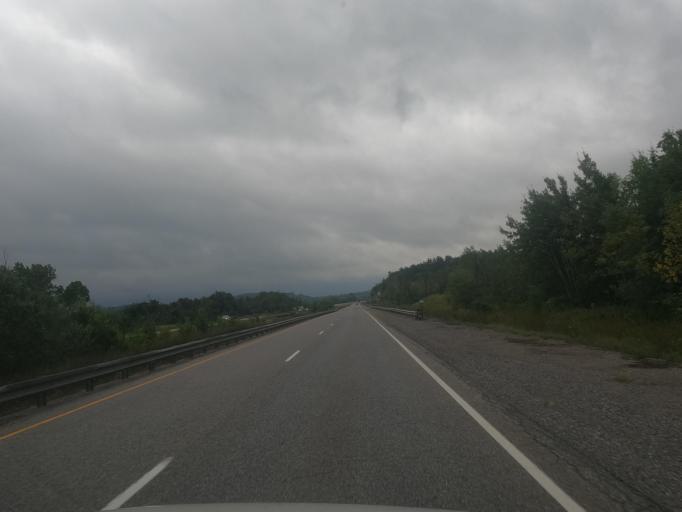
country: CA
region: Ontario
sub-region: Algoma
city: Sault Ste. Marie
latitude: 46.5092
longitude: -84.0492
